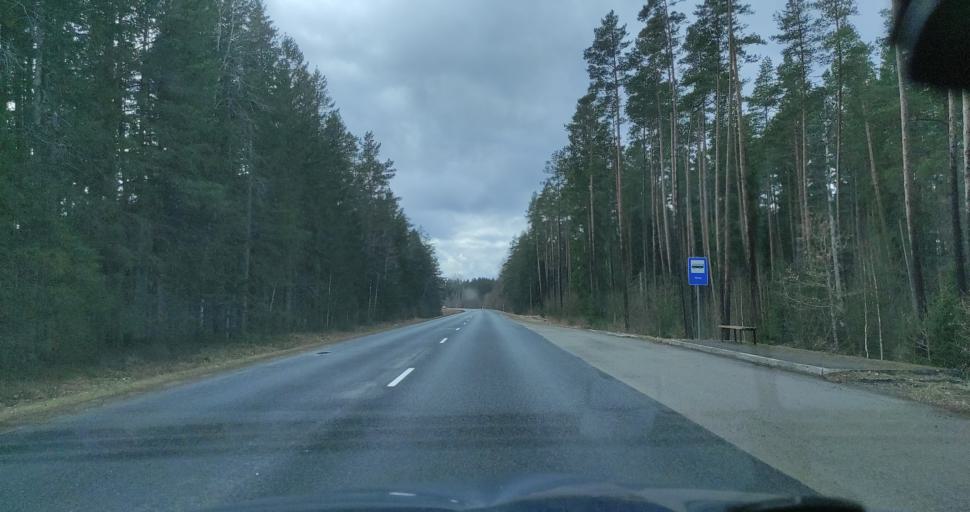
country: LV
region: Talsu Rajons
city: Stende
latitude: 57.1074
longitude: 22.4934
